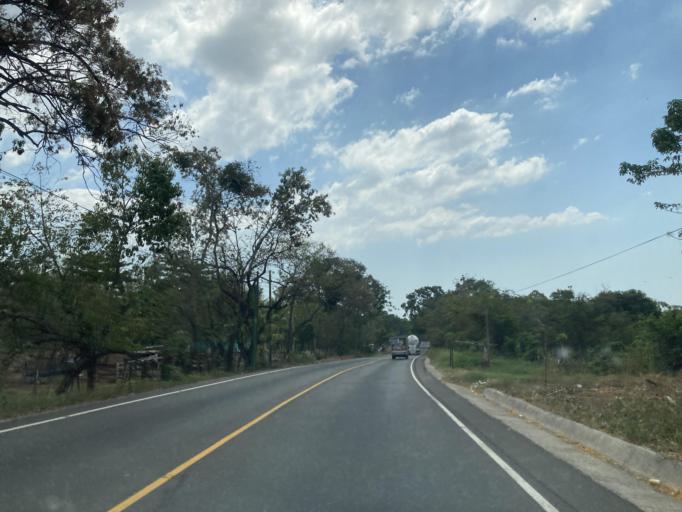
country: GT
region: Santa Rosa
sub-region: Municipio de Taxisco
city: Taxisco
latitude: 14.0879
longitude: -90.4957
